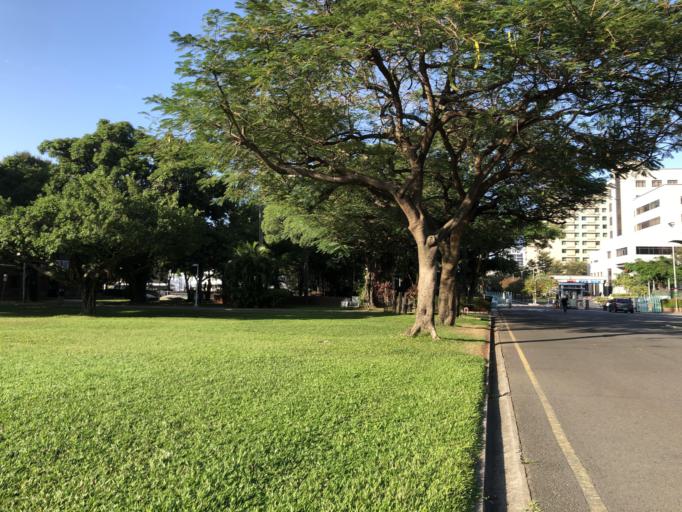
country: TW
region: Taiwan
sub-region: Tainan
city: Tainan
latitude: 23.0003
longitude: 120.2168
